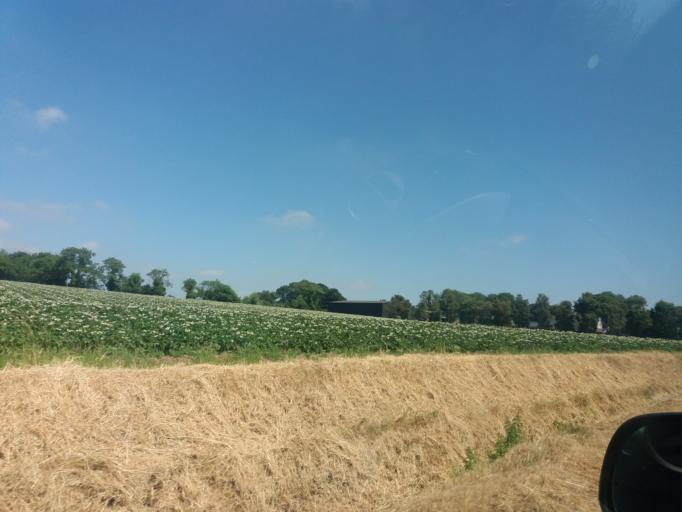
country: IE
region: Leinster
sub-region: Fingal County
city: Swords
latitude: 53.5166
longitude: -6.2497
